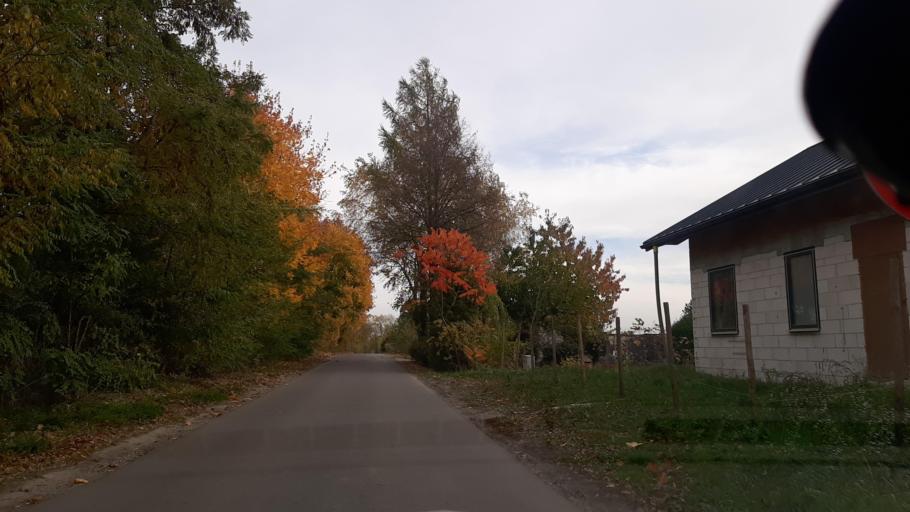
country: PL
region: Lublin Voivodeship
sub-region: Powiat pulawski
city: Naleczow
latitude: 51.3123
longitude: 22.2154
